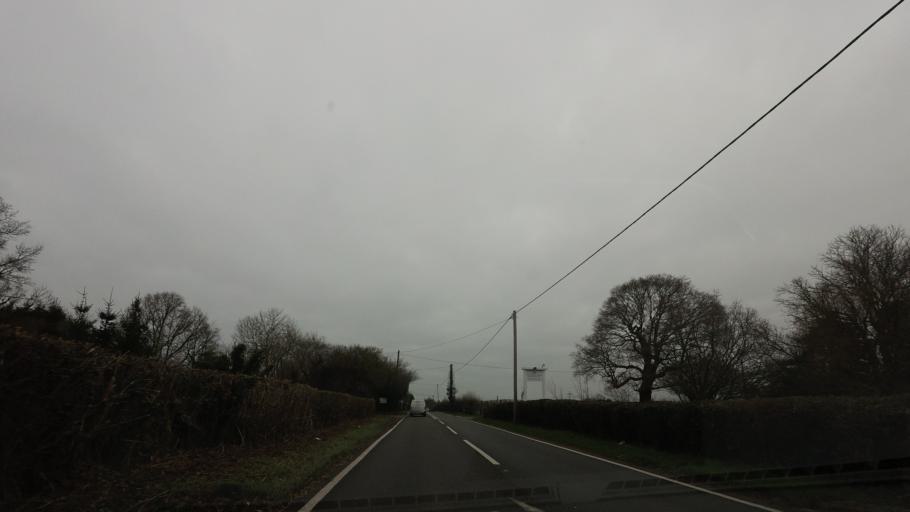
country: GB
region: England
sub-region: East Sussex
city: Saint Leonards-on-Sea
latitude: 50.9096
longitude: 0.5458
